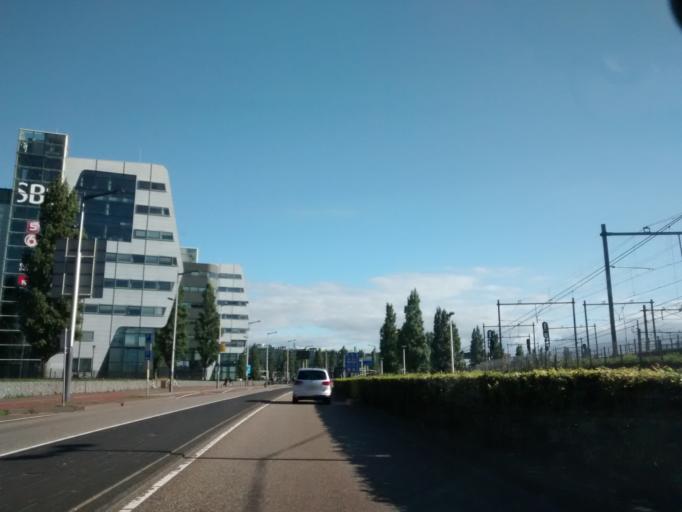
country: NL
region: North Holland
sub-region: Gemeente Amsterdam
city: Amsterdam
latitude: 52.3745
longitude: 4.9305
